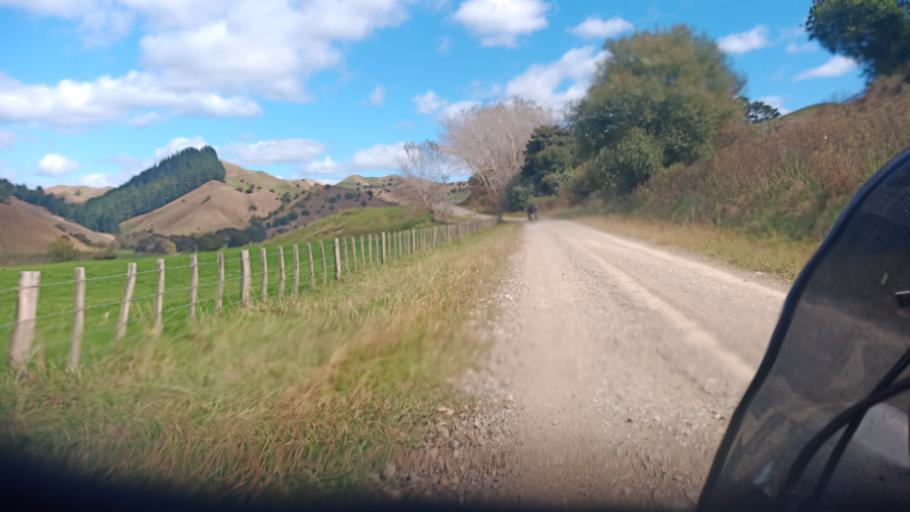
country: NZ
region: Gisborne
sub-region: Gisborne District
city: Gisborne
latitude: -38.4245
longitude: 177.7178
